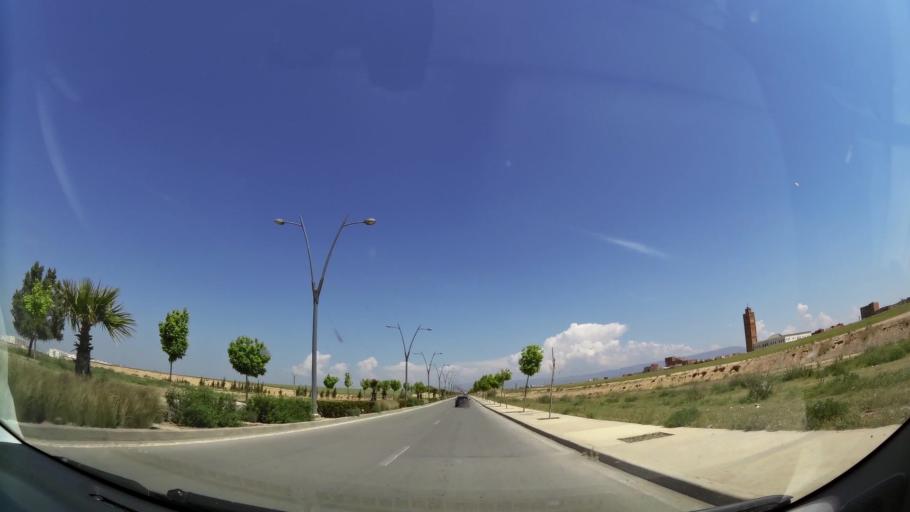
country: MA
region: Oriental
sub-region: Oujda-Angad
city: Oujda
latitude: 34.6968
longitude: -1.9399
